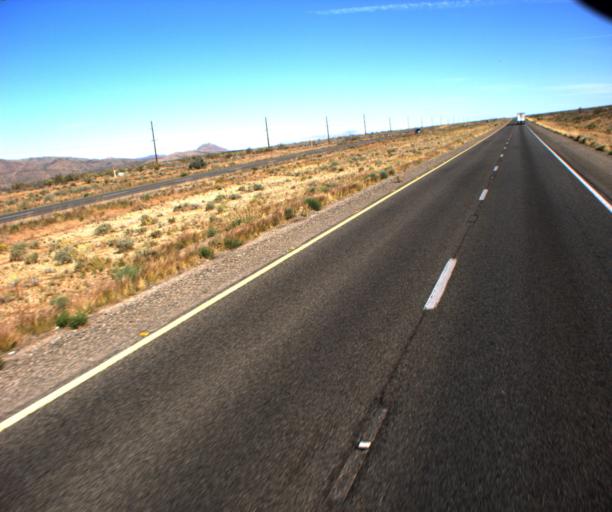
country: US
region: Arizona
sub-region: Mohave County
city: Golden Valley
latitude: 35.3413
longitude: -114.2189
